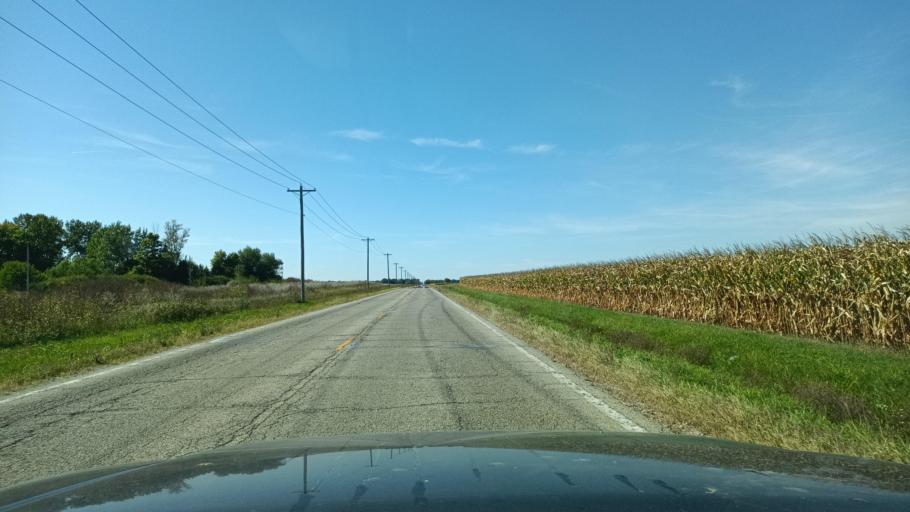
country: US
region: Illinois
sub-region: Champaign County
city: Mahomet
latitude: 40.2040
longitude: -88.4646
